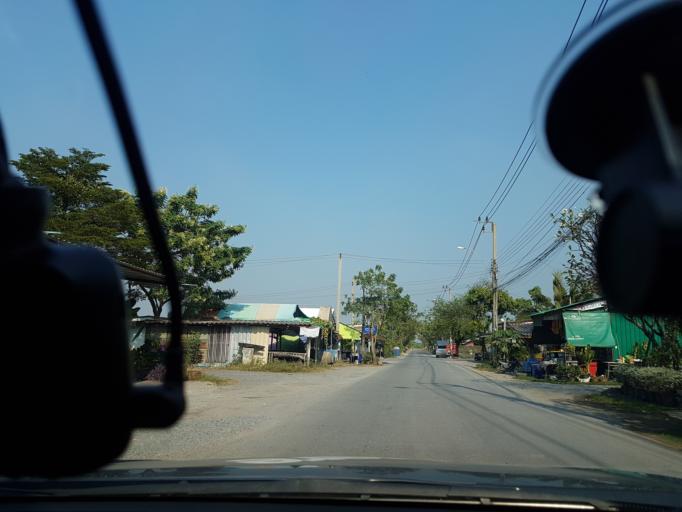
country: TH
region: Pathum Thani
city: Lam Luk Ka
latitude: 13.9122
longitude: 100.7073
